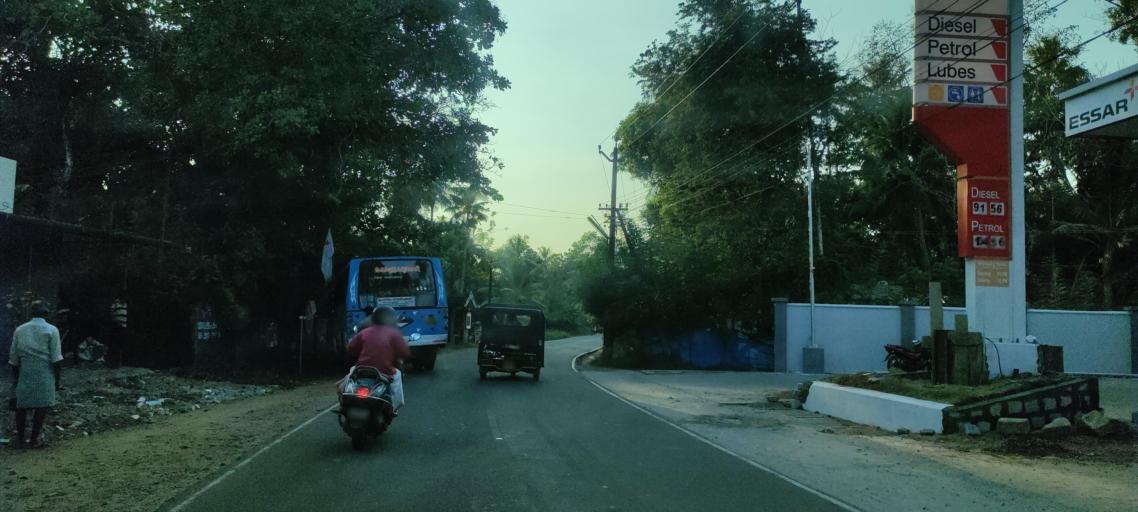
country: IN
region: Kerala
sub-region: Alappuzha
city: Kutiatodu
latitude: 9.7730
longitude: 76.3471
